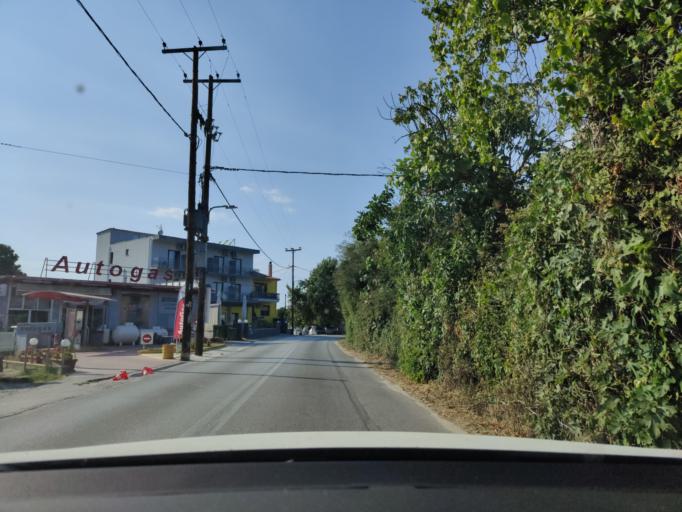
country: GR
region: East Macedonia and Thrace
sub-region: Nomos Kavalas
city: Prinos
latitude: 40.7569
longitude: 24.5778
